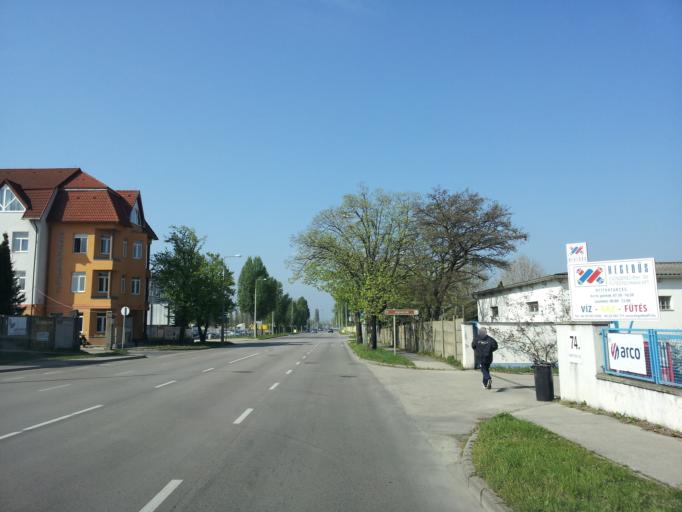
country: HU
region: Fejer
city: Szekesfehervar
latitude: 47.1892
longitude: 18.4431
